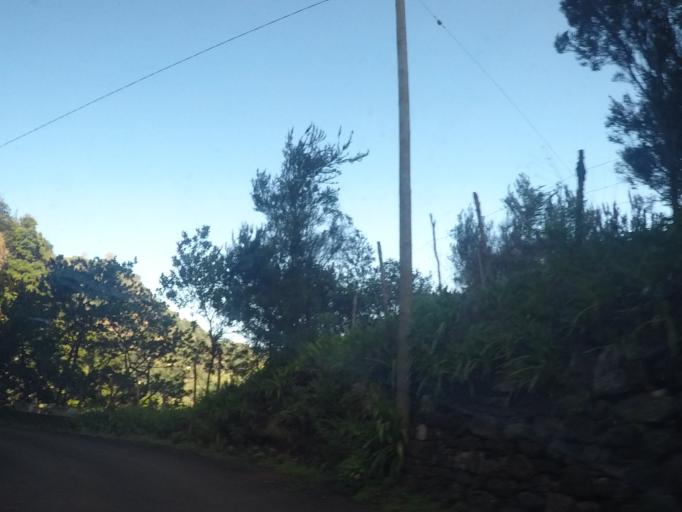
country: PT
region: Madeira
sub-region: Santana
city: Santana
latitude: 32.8160
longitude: -16.8951
